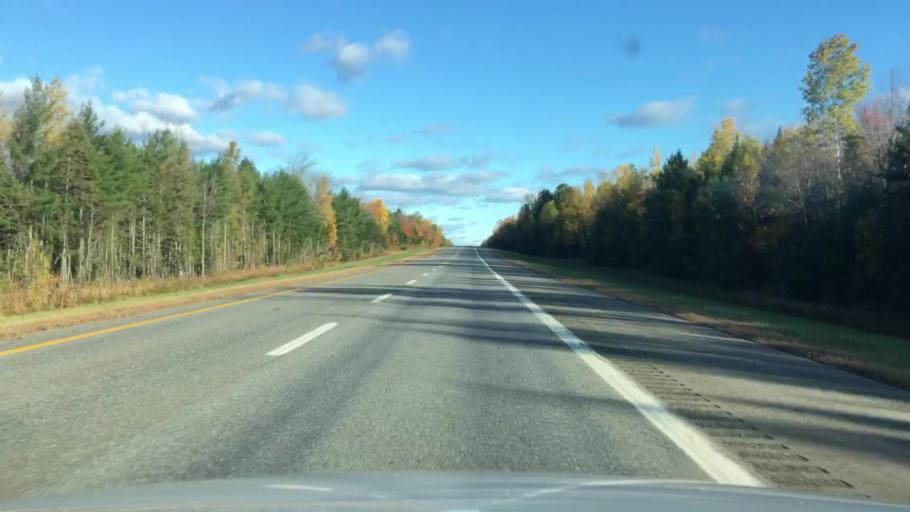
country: US
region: Maine
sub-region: Penobscot County
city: Greenbush
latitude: 45.0648
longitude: -68.6892
